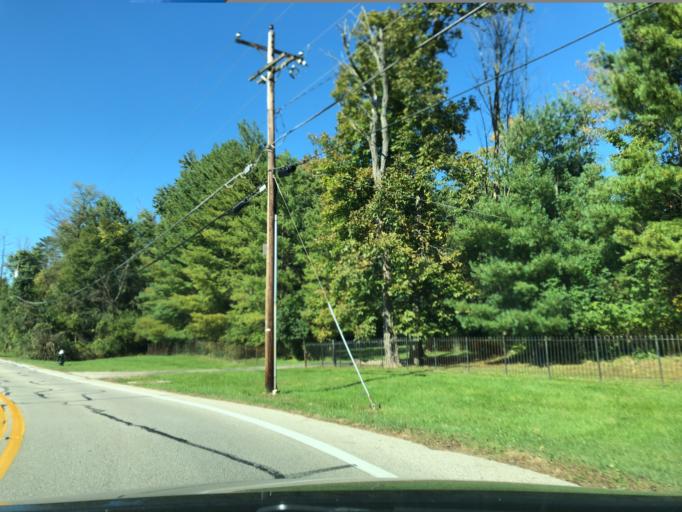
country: US
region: Ohio
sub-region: Hamilton County
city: Sixteen Mile Stand
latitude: 39.2744
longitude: -84.3062
